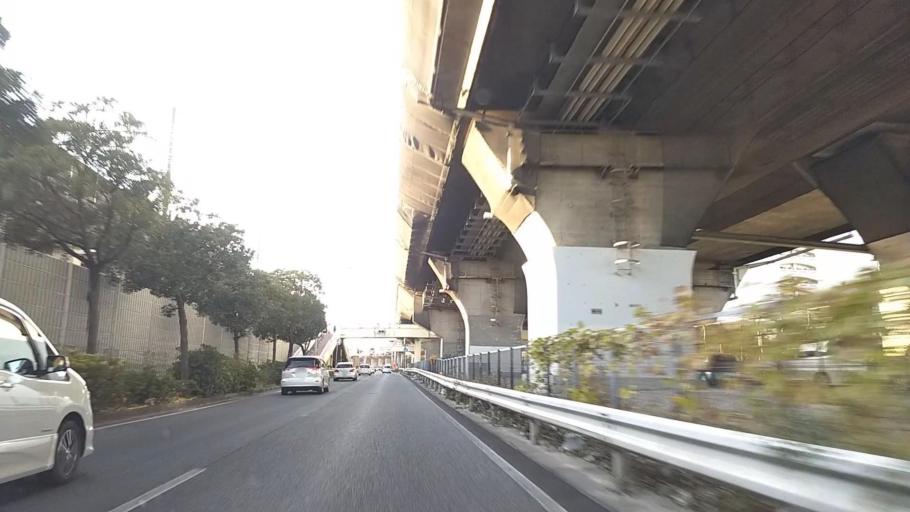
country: JP
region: Chiba
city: Funabashi
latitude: 35.6832
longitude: 139.9936
